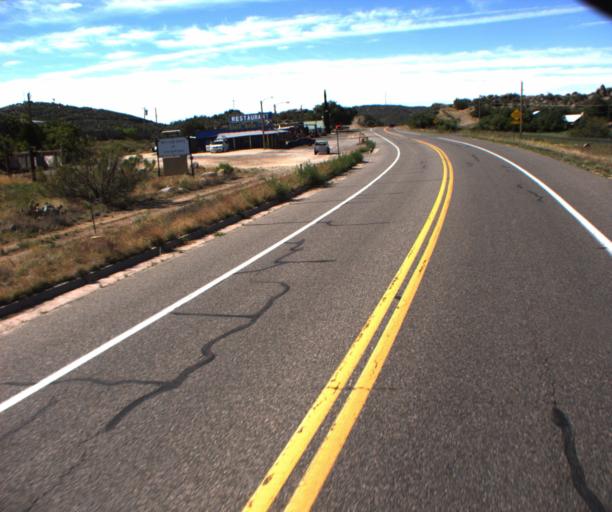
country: US
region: Arizona
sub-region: Yavapai County
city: Congress
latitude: 34.2139
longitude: -112.7555
